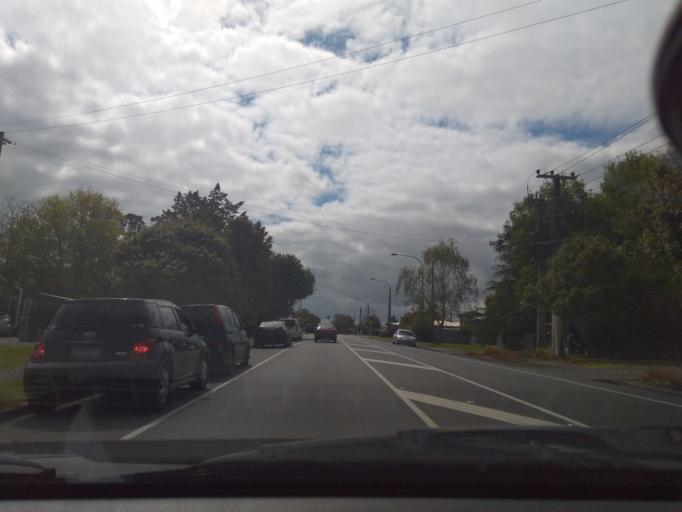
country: NZ
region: Auckland
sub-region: Auckland
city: Rosebank
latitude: -36.8641
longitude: 174.5997
